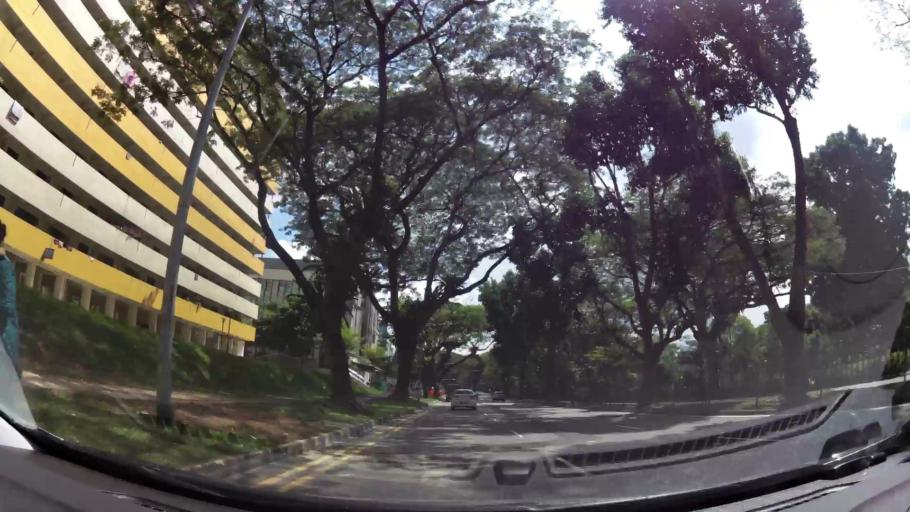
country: SG
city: Singapore
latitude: 1.3670
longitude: 103.8345
